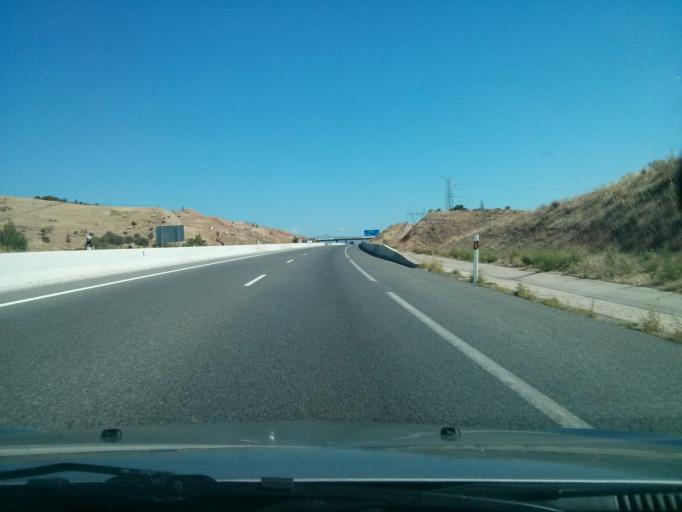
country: ES
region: Madrid
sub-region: Provincia de Madrid
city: El Molar
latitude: 40.7242
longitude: -3.5763
